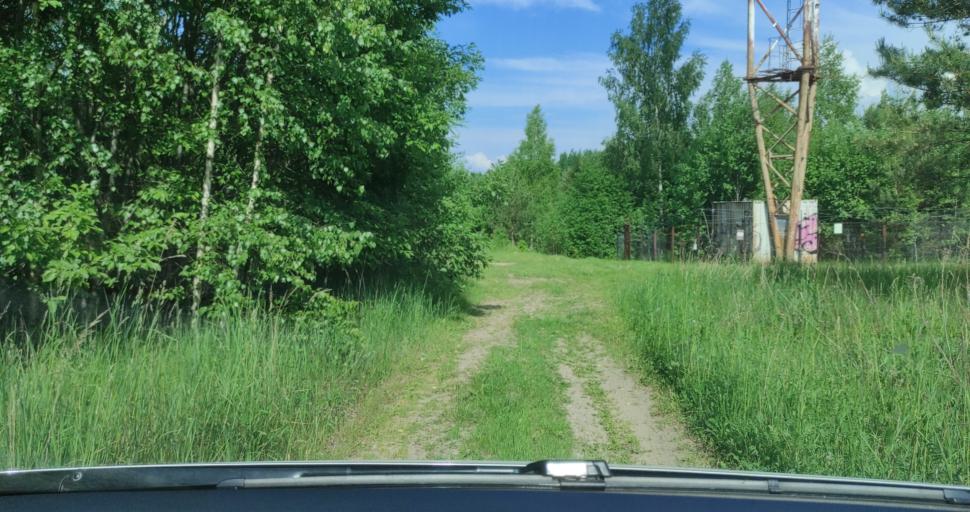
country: LV
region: Kuldigas Rajons
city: Kuldiga
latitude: 56.9372
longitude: 21.9218
